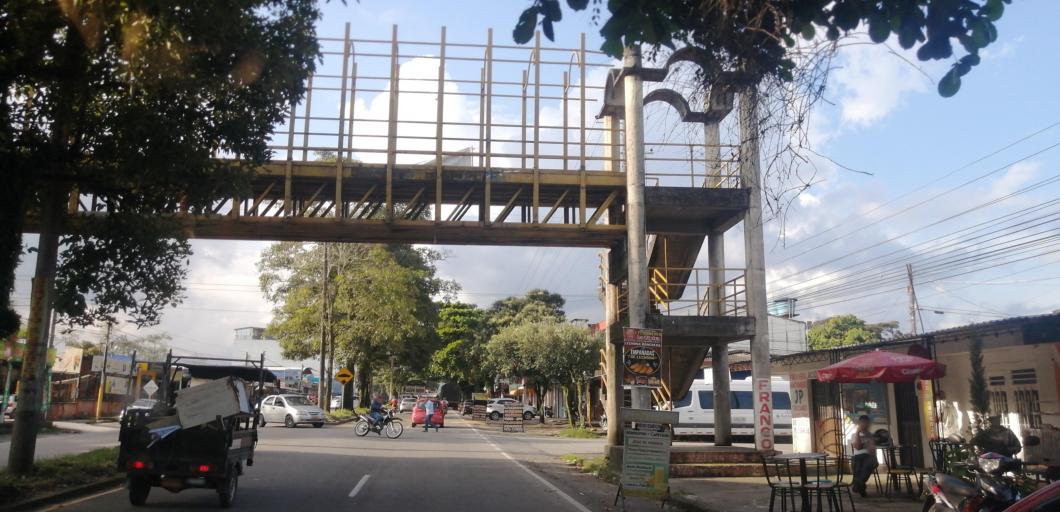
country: CO
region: Meta
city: Acacias
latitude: 3.9811
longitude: -73.7667
